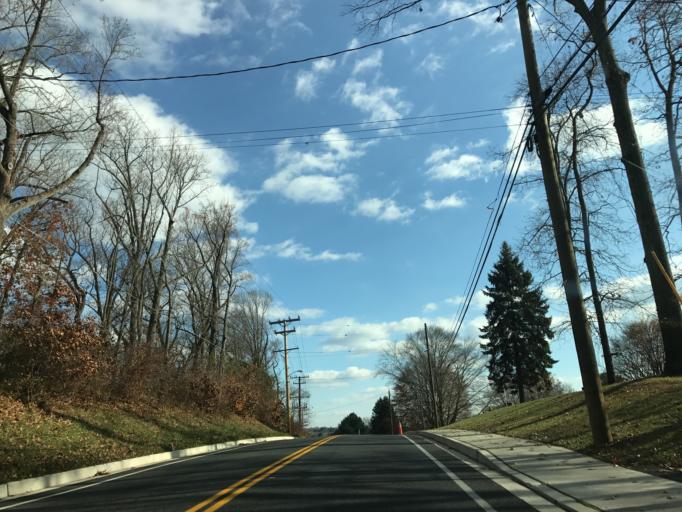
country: US
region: Maryland
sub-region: Harford County
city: South Bel Air
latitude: 39.5495
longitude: -76.3387
